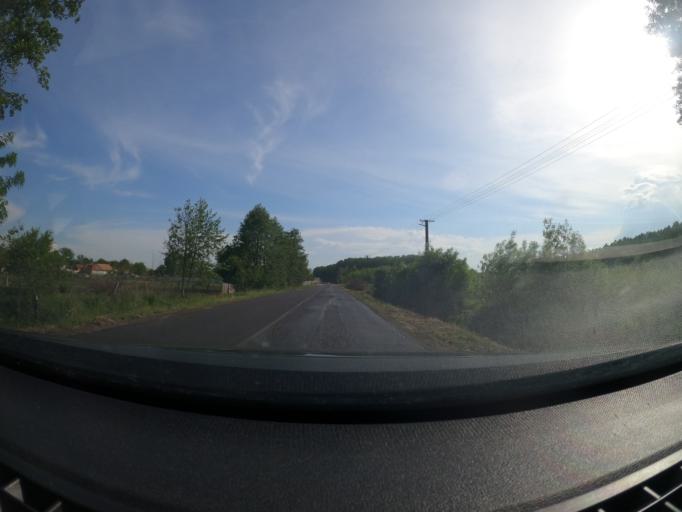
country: HU
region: Hajdu-Bihar
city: Nyirabrany
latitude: 47.5271
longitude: 21.9849
